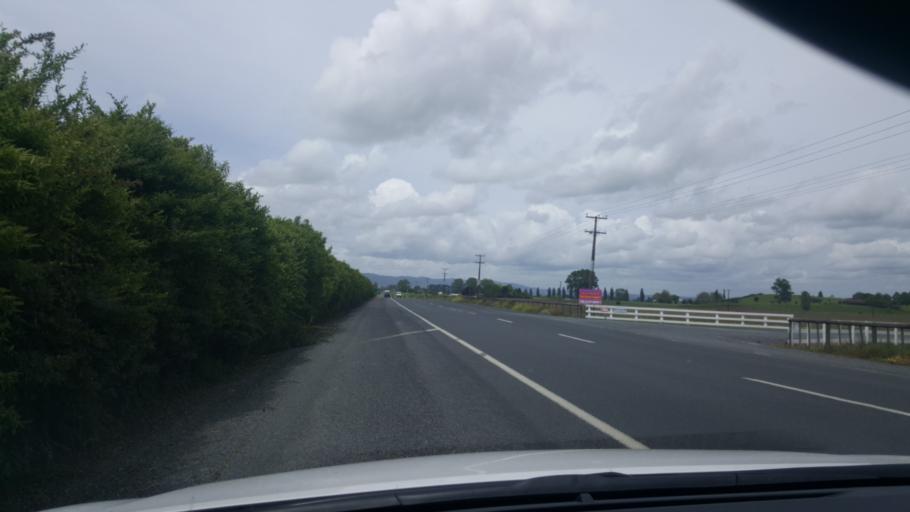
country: NZ
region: Waikato
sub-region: Matamata-Piako District
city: Matamata
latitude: -37.8864
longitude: 175.7691
